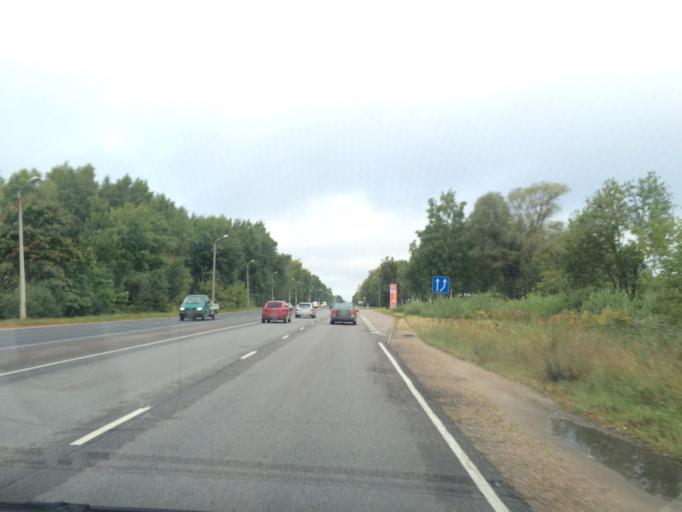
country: LV
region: Kekava
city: Kekava
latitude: 56.8808
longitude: 24.2494
